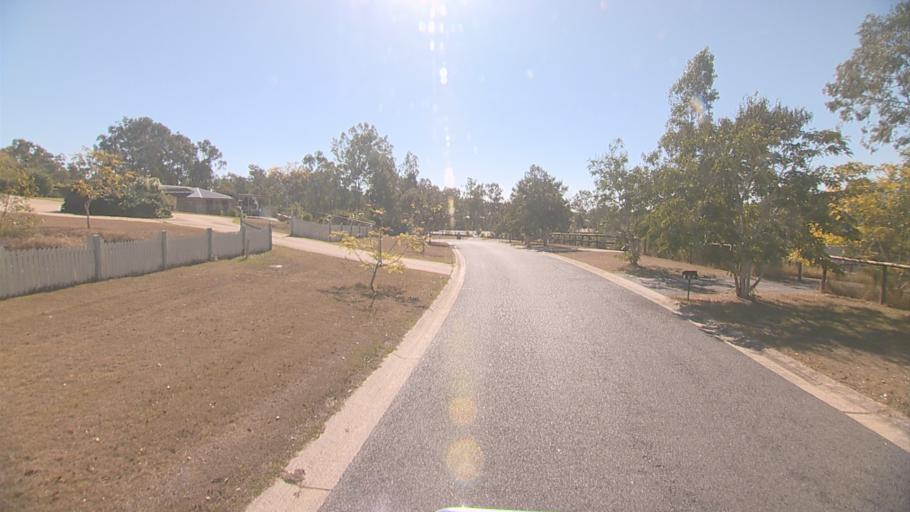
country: AU
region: Queensland
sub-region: Logan
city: Cedar Vale
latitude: -27.8678
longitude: 153.0388
